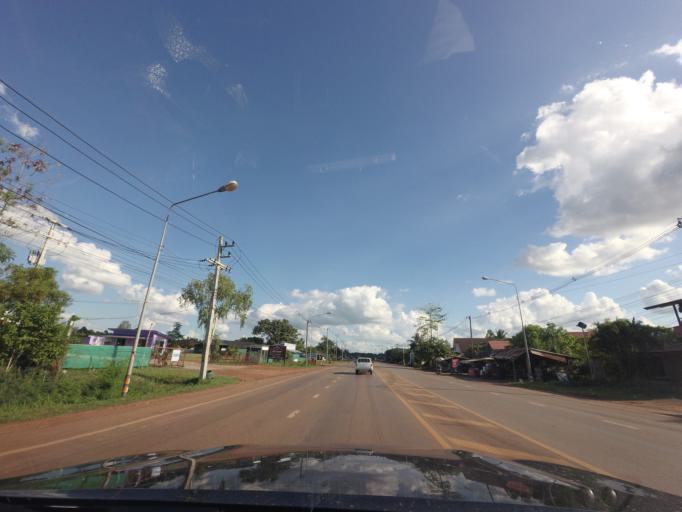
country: TH
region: Changwat Udon Thani
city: Ban Dung
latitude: 17.7080
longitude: 103.2510
